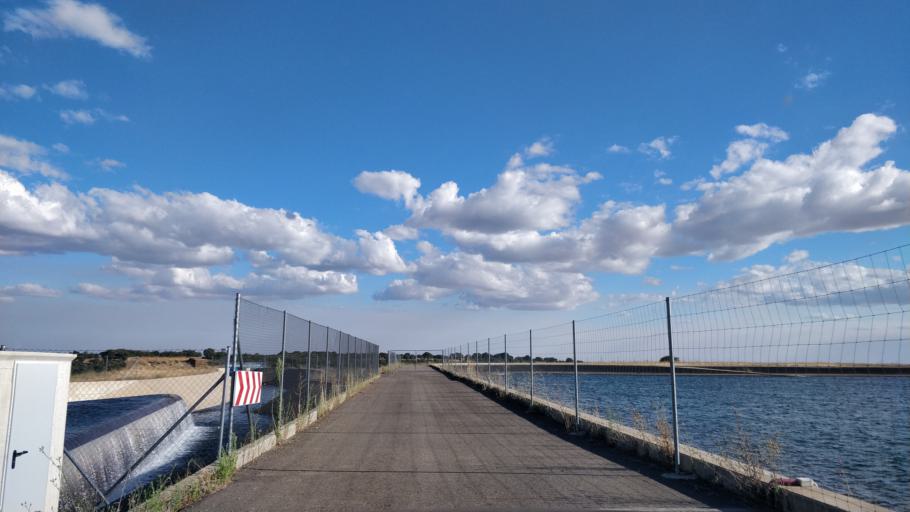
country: ES
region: Castille and Leon
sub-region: Provincia de Leon
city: Santa Cristina de Valmadrigal
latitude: 42.3470
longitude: -5.2642
